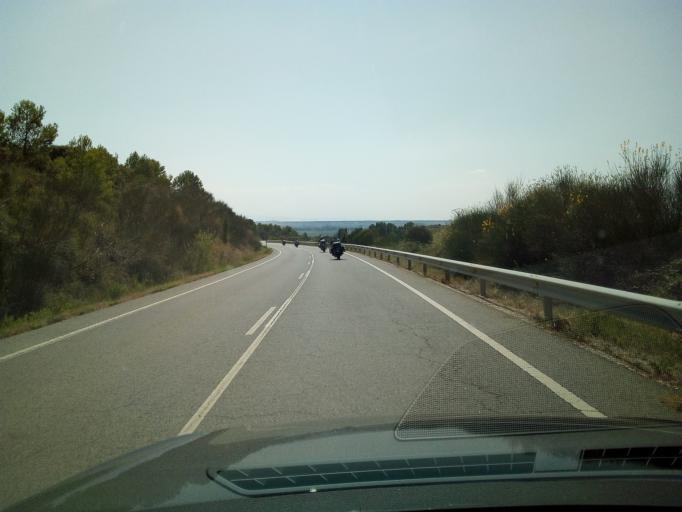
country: ES
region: Navarre
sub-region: Provincia de Navarra
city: San Martin de Unx
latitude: 42.4983
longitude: -1.5903
